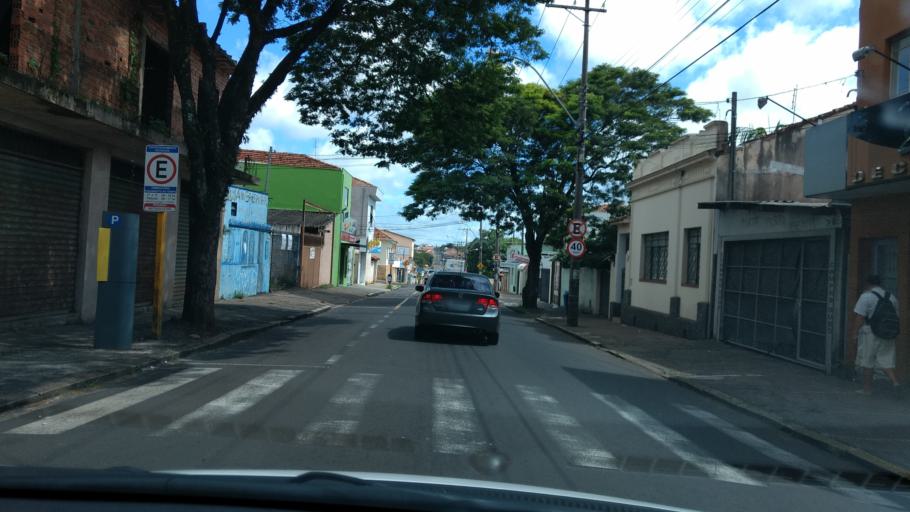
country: BR
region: Sao Paulo
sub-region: Botucatu
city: Botucatu
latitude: -22.8852
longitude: -48.4398
